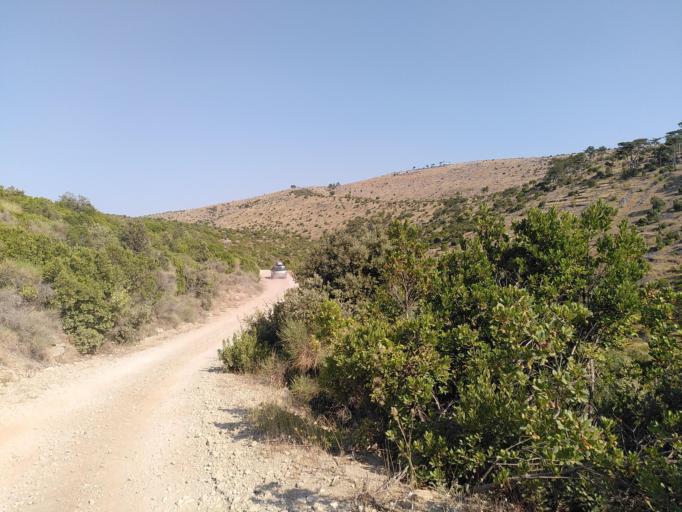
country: HR
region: Splitsko-Dalmatinska
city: Stari Grad
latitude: 43.1528
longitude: 16.5751
